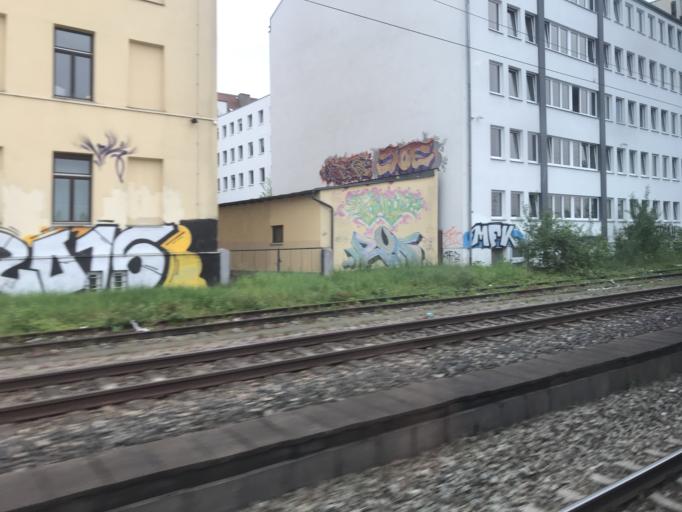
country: DE
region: Bavaria
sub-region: Upper Bavaria
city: Pasing
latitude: 48.1447
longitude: 11.4961
